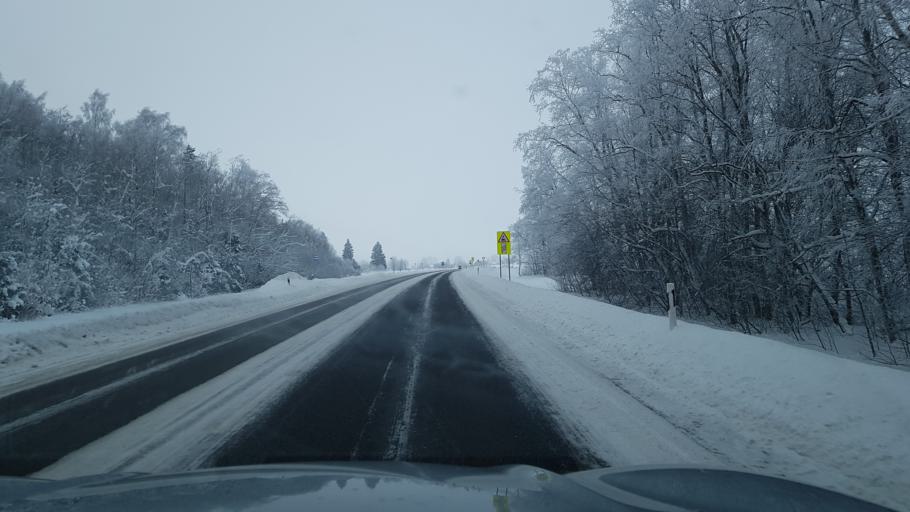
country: EE
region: Ida-Virumaa
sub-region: Johvi vald
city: Johvi
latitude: 59.3074
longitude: 27.3931
